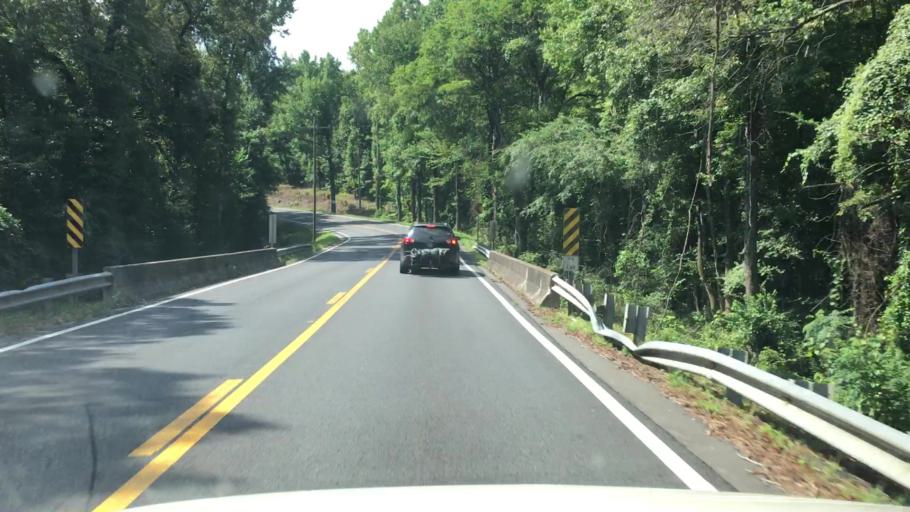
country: US
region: Arkansas
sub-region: Clark County
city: Arkadelphia
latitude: 34.2585
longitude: -93.1303
